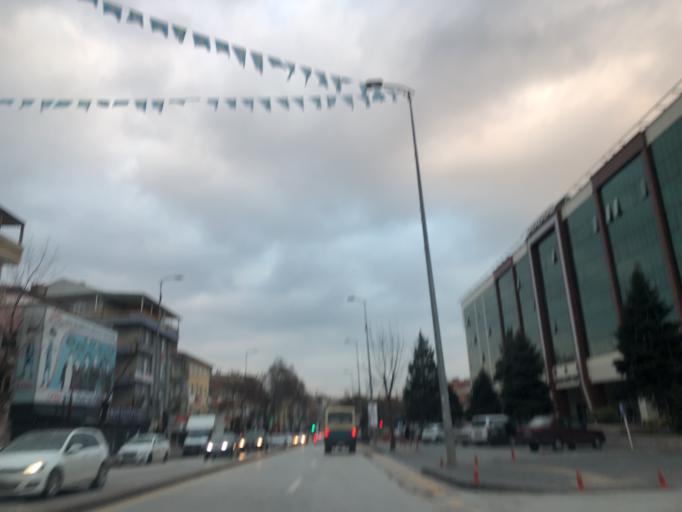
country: TR
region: Ankara
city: Ankara
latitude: 39.9628
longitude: 32.8094
